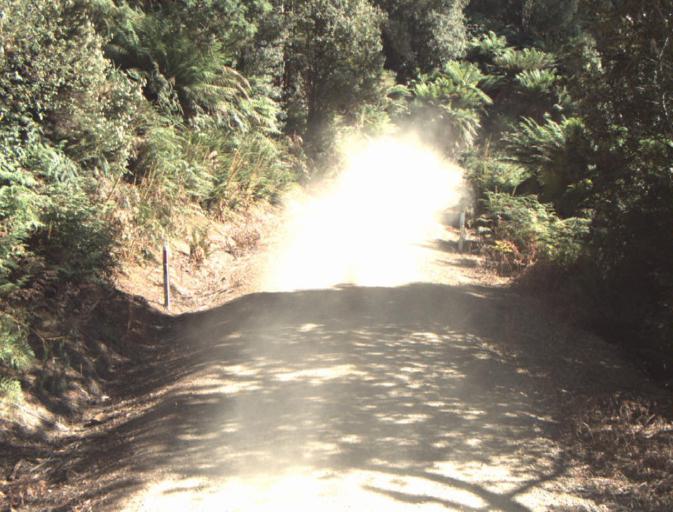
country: AU
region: Tasmania
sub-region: Dorset
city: Scottsdale
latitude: -41.2732
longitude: 147.3636
